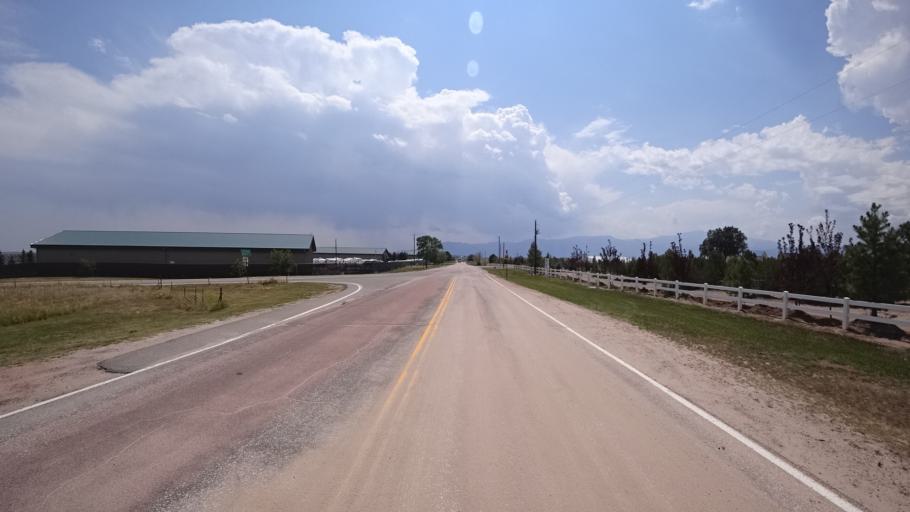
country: US
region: Colorado
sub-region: El Paso County
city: Black Forest
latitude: 38.9396
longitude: -104.7062
